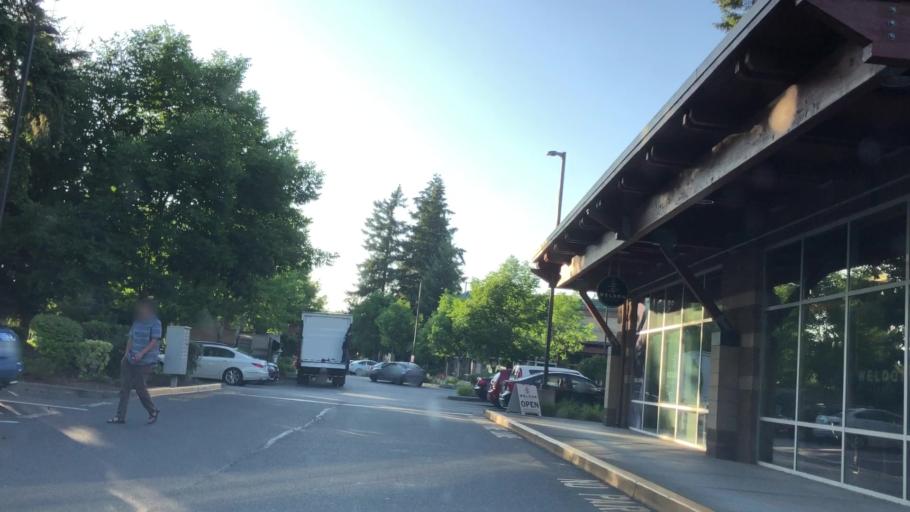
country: US
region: Washington
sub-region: King County
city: Redmond
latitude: 47.6667
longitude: -122.1029
